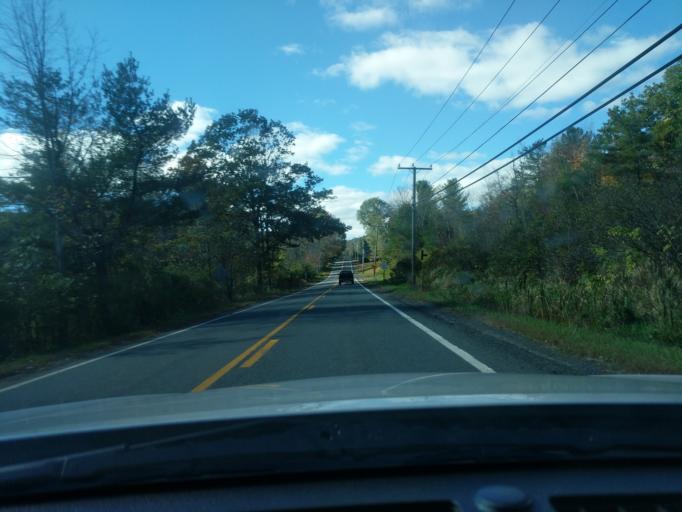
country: US
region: Massachusetts
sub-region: Hampden County
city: Granville
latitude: 42.1684
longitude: -72.8746
